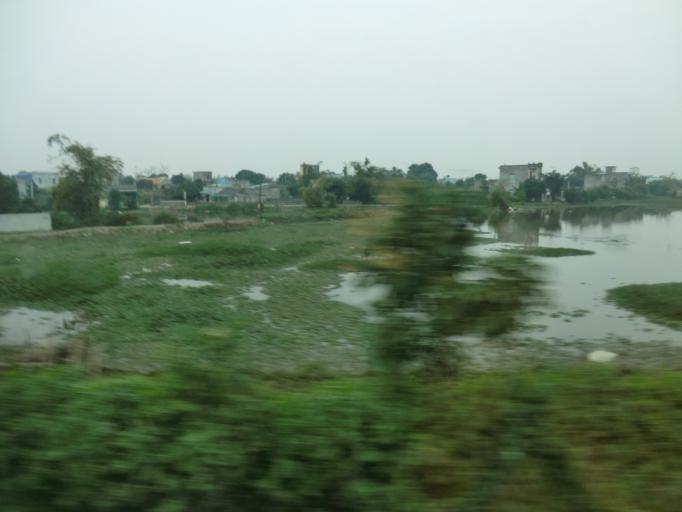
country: VN
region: Nam Dinh
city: Thanh Pho Nam Dinh
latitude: 20.4015
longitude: 106.1505
